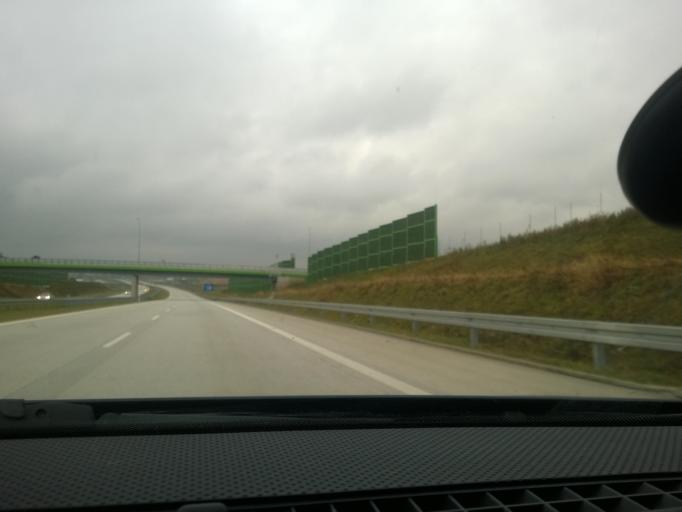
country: PL
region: Lodz Voivodeship
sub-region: Powiat zgierski
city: Strykow
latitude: 51.8323
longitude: 19.6555
